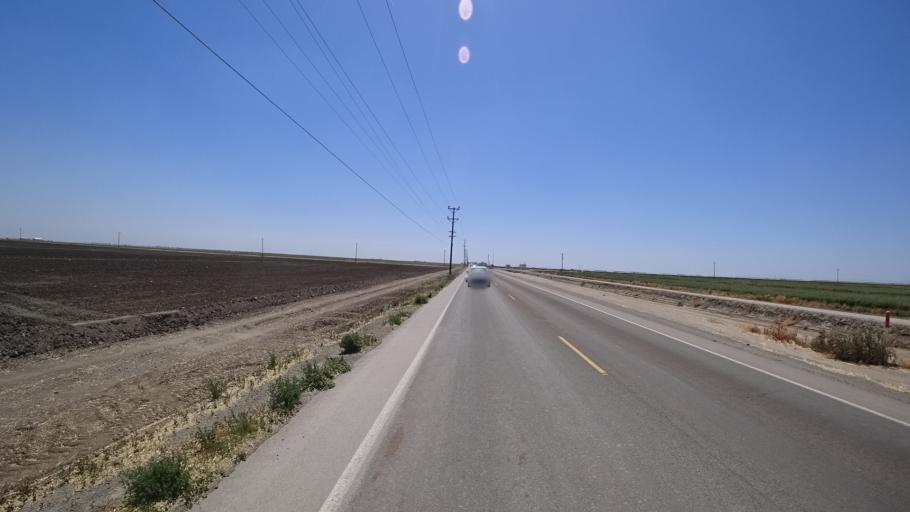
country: US
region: California
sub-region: Kings County
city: Corcoran
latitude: 36.1694
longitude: -119.6459
